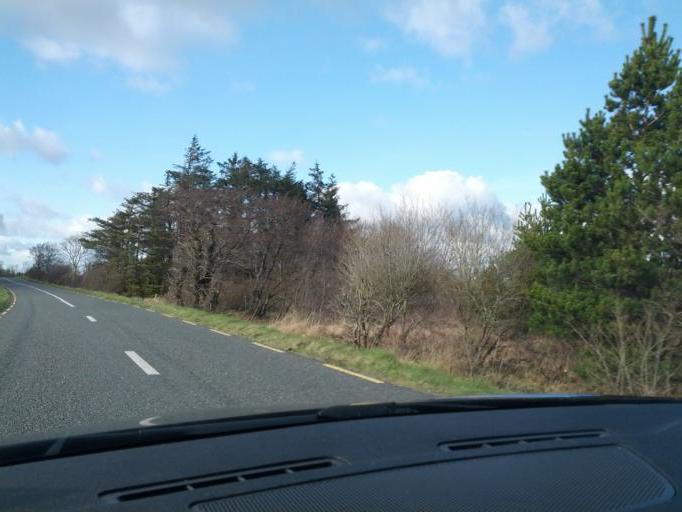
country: IE
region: Connaught
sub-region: County Galway
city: Athenry
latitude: 53.5029
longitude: -8.5715
